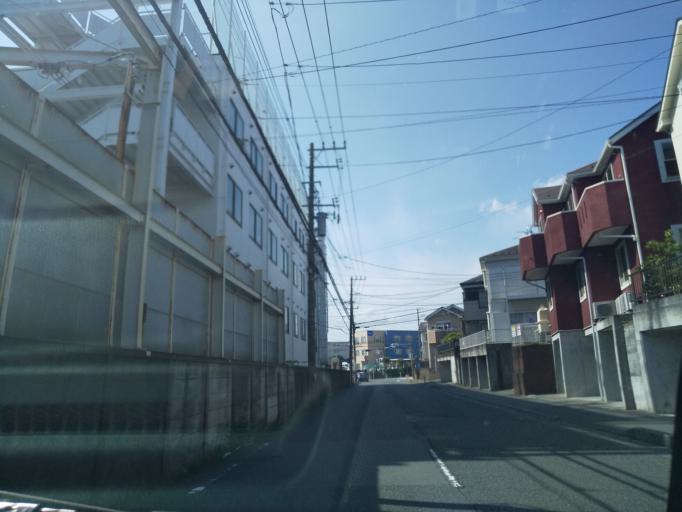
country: JP
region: Kanagawa
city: Zama
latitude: 35.4600
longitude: 139.4146
